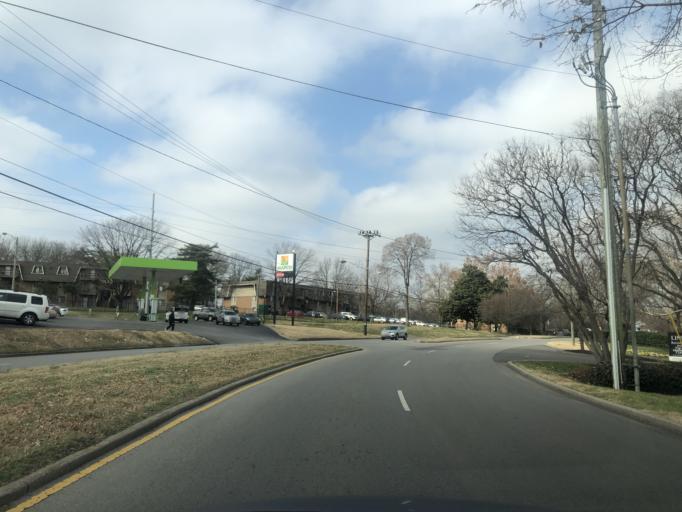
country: US
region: Tennessee
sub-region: Davidson County
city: Oak Hill
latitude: 36.0813
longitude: -86.7013
